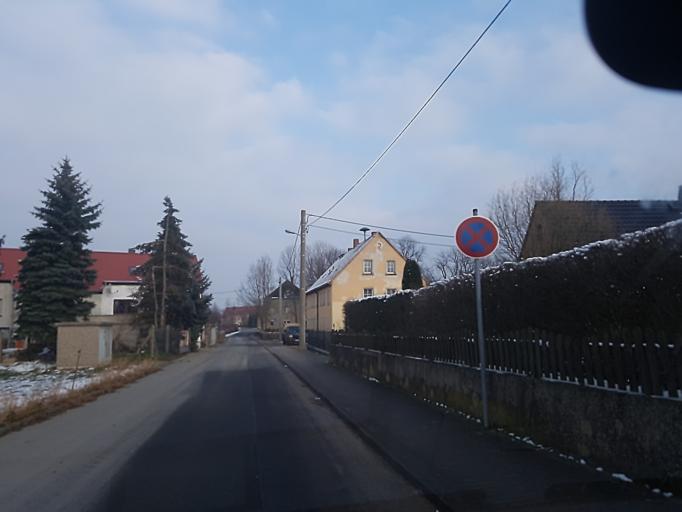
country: DE
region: Saxony
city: Oschatz
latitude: 51.3420
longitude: 13.0920
